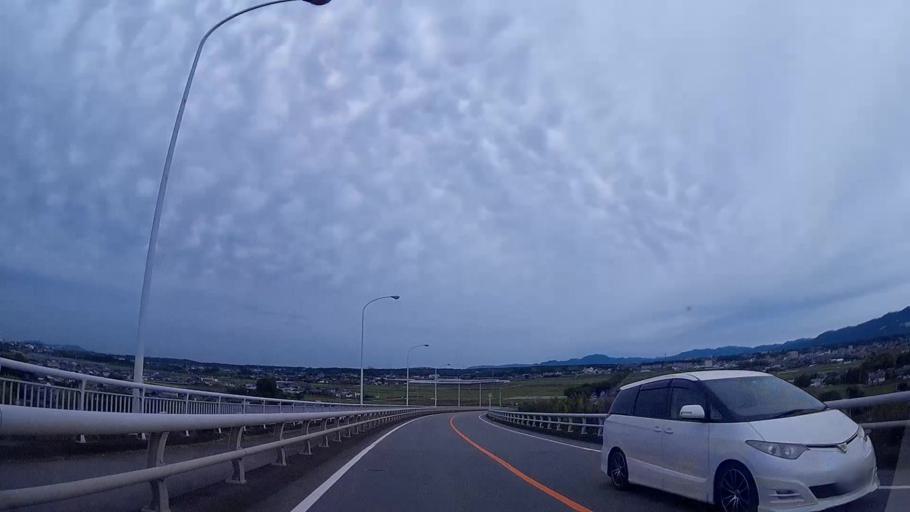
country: JP
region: Kumamoto
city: Ozu
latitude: 32.8526
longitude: 130.8557
